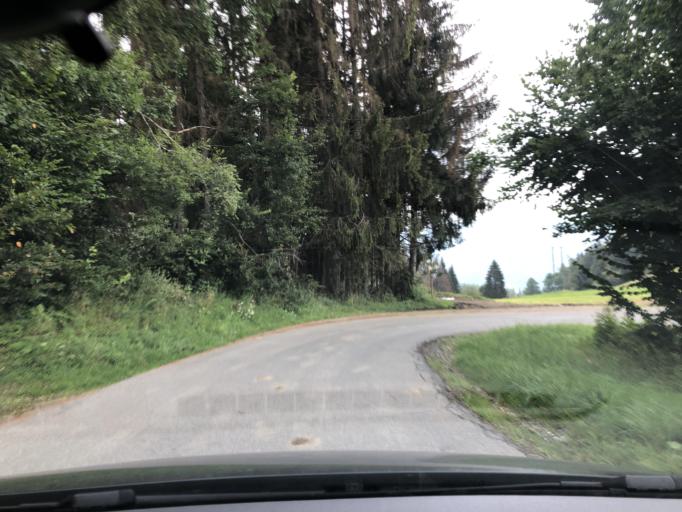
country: FR
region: Rhone-Alpes
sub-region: Departement de la Haute-Savoie
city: Combloux
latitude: 45.9026
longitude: 6.6189
